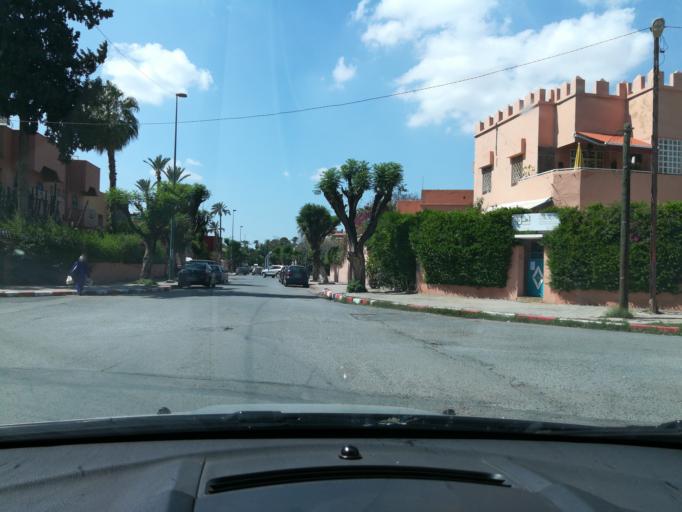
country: MA
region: Marrakech-Tensift-Al Haouz
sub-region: Marrakech
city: Marrakesh
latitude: 31.6388
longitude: -8.0138
